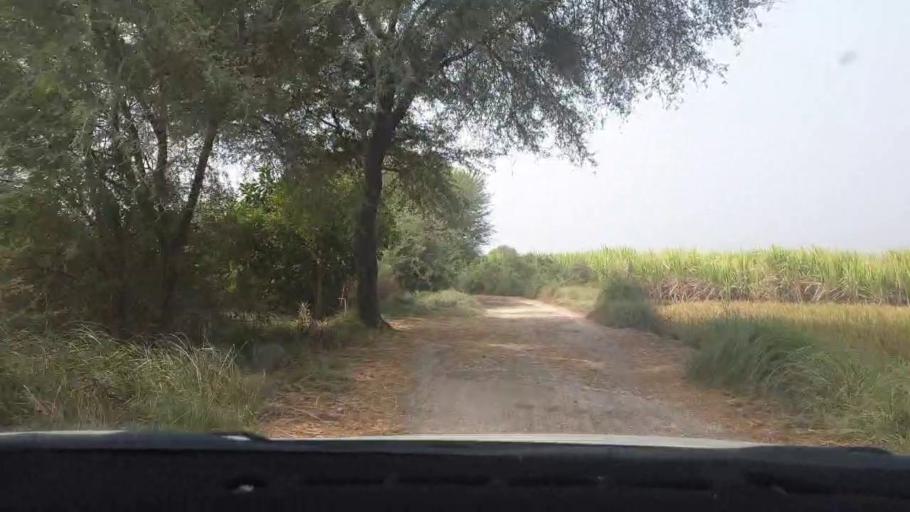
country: PK
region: Sindh
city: Tando Muhammad Khan
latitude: 25.0192
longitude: 68.5343
